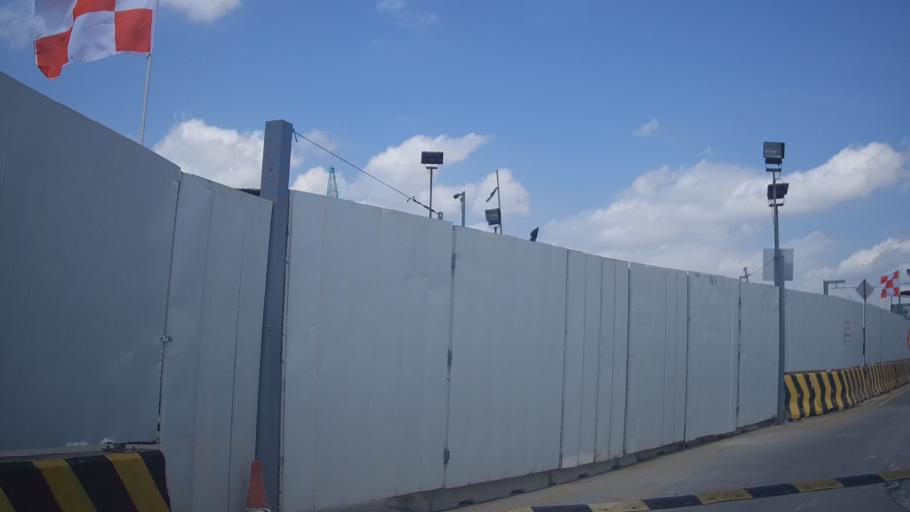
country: SG
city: Singapore
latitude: 1.3238
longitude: 103.9619
